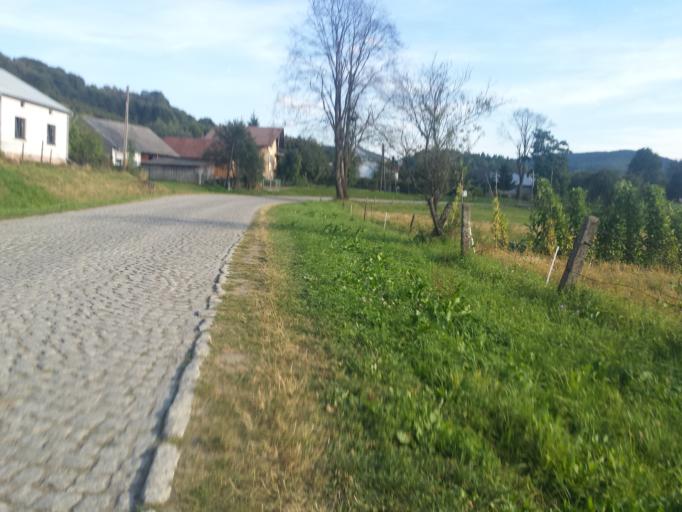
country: PL
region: Subcarpathian Voivodeship
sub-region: Powiat leski
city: Uherce Mineralne
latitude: 49.4396
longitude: 22.4101
